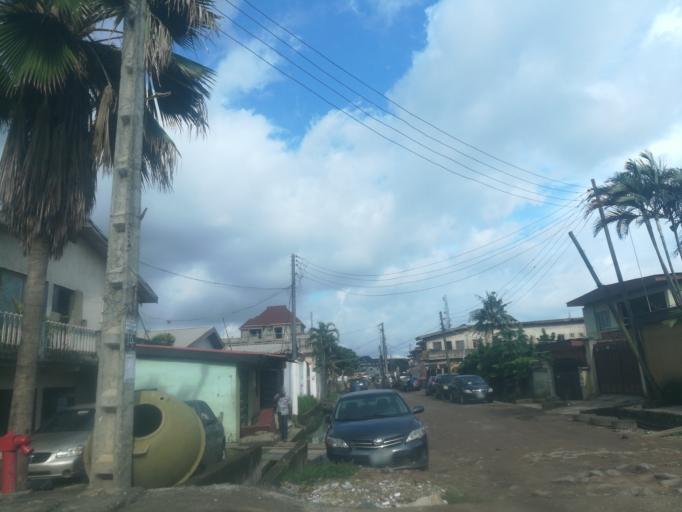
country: NG
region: Lagos
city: Somolu
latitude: 6.5430
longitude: 3.3758
